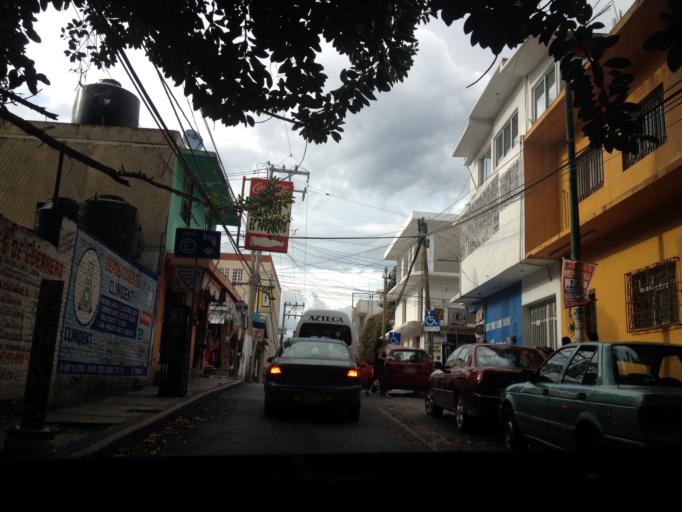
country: MX
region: Guerrero
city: Chilpancingo de los Bravos
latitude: 17.5517
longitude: -99.5029
